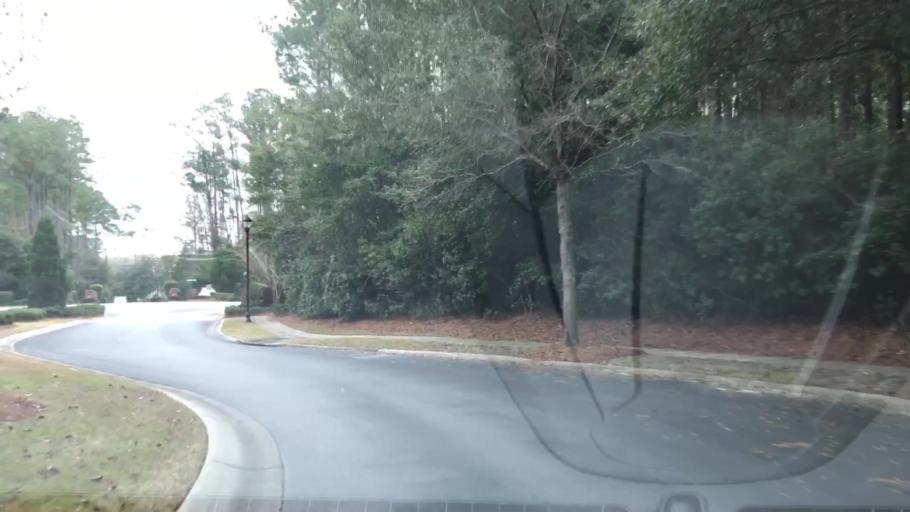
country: US
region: South Carolina
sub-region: Beaufort County
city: Bluffton
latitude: 32.2759
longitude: -80.9283
